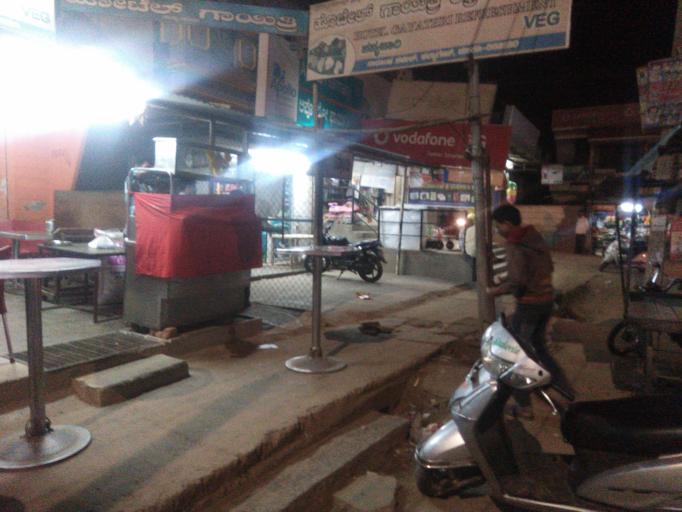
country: IN
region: Karnataka
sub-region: Ramanagara
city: Magadi
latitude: 12.9580
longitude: 77.2215
